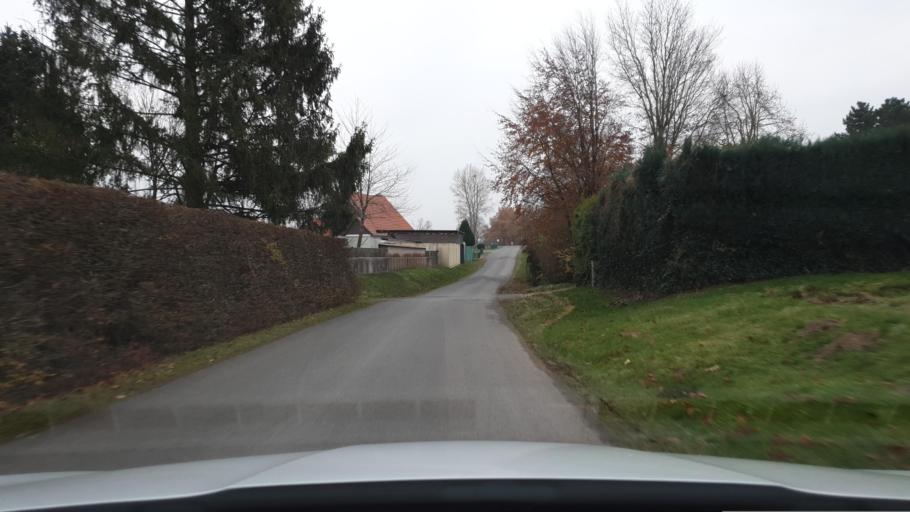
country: DE
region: North Rhine-Westphalia
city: Bad Oeynhausen
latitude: 52.1677
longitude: 8.8094
